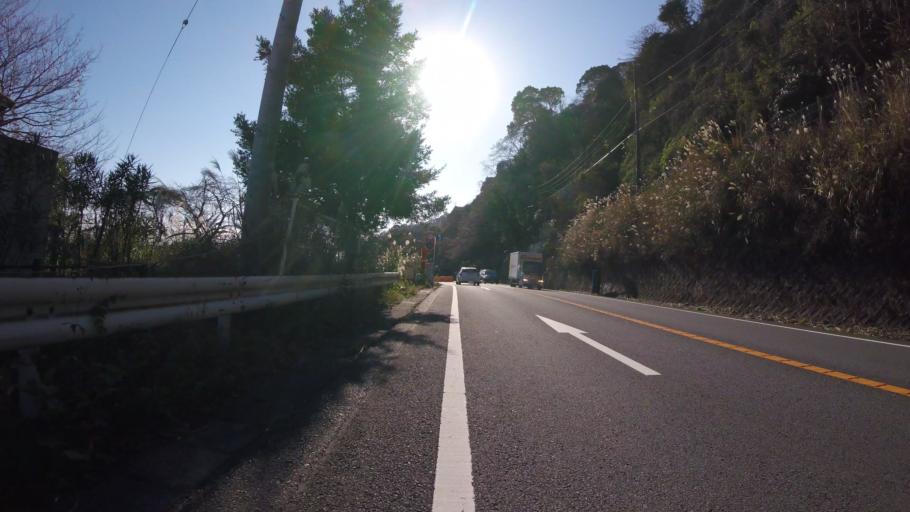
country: JP
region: Shizuoka
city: Atami
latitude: 35.0757
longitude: 139.0744
